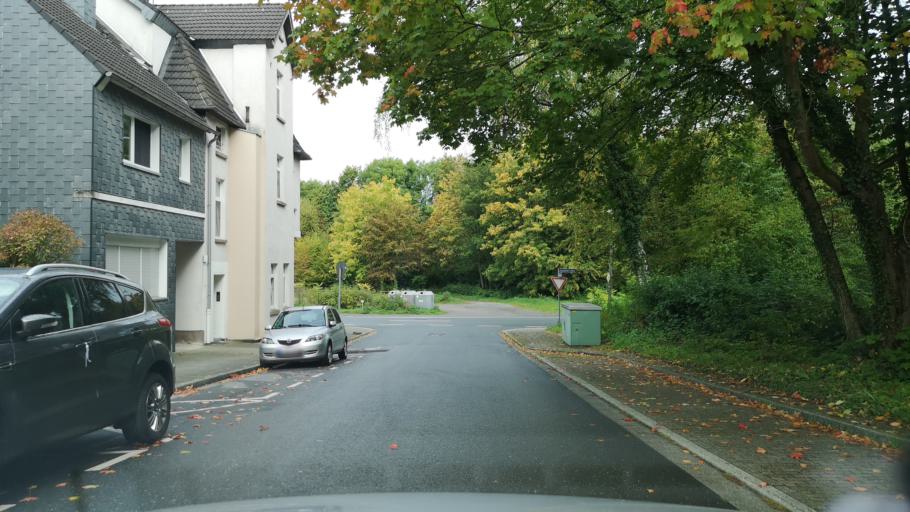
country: DE
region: North Rhine-Westphalia
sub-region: Regierungsbezirk Dusseldorf
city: Heiligenhaus
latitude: 51.3787
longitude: 6.9931
